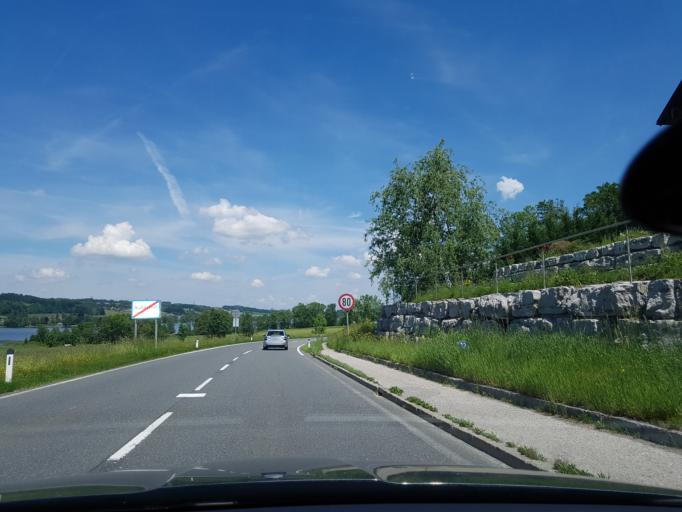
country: AT
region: Salzburg
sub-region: Politischer Bezirk Salzburg-Umgebung
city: Obertrum am See
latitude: 47.9447
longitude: 13.0882
